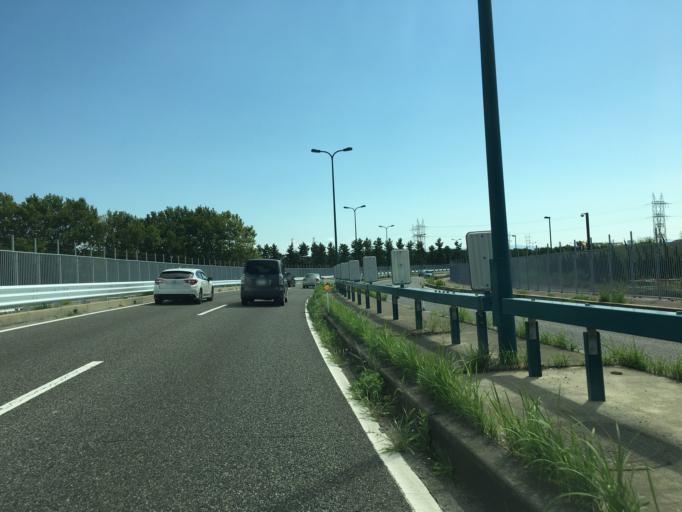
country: JP
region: Niigata
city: Niigata-shi
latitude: 37.9469
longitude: 139.0843
